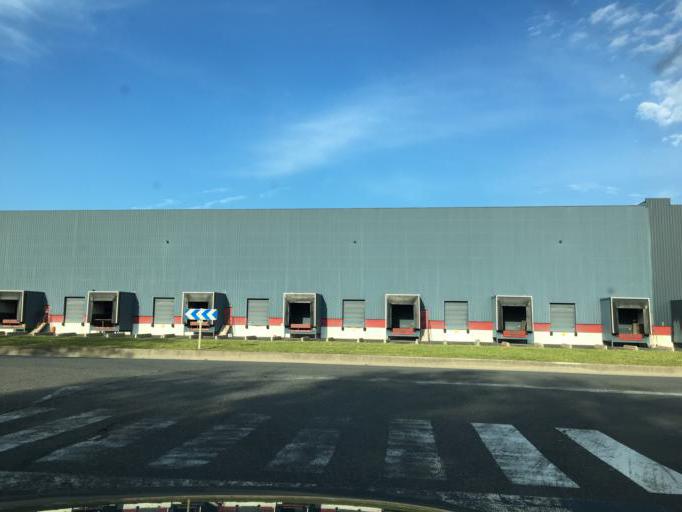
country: FR
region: Centre
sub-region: Departement du Loiret
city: Ormes
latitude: 47.9459
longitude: 1.8442
